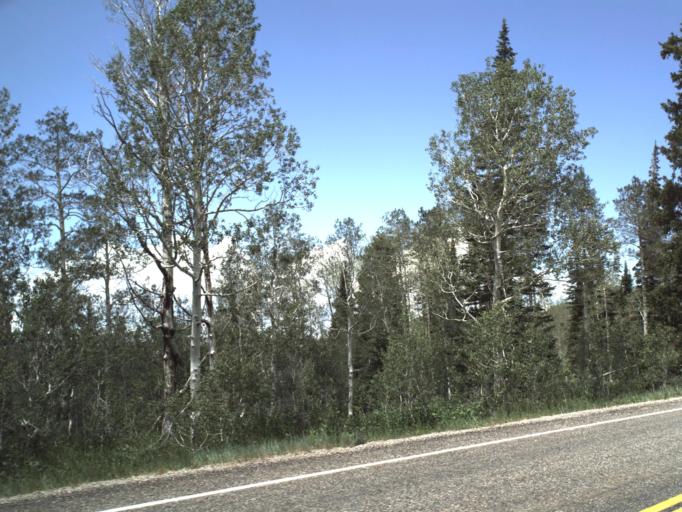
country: US
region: Utah
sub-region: Weber County
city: Wolf Creek
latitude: 41.4669
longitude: -111.4924
